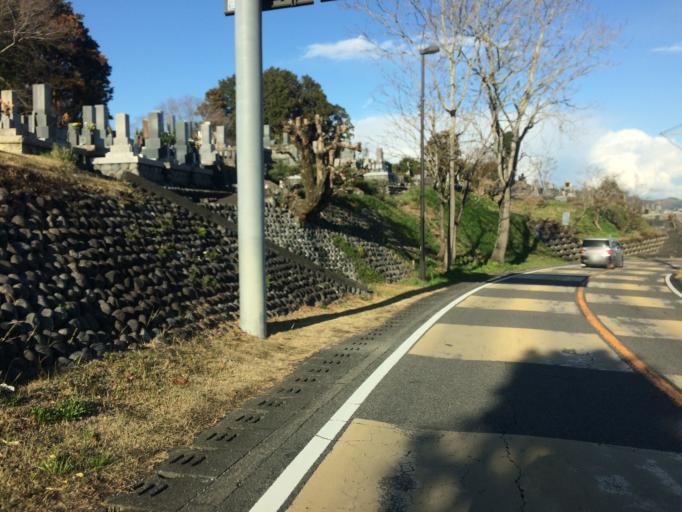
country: JP
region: Shizuoka
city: Kanaya
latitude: 34.8236
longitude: 138.1266
